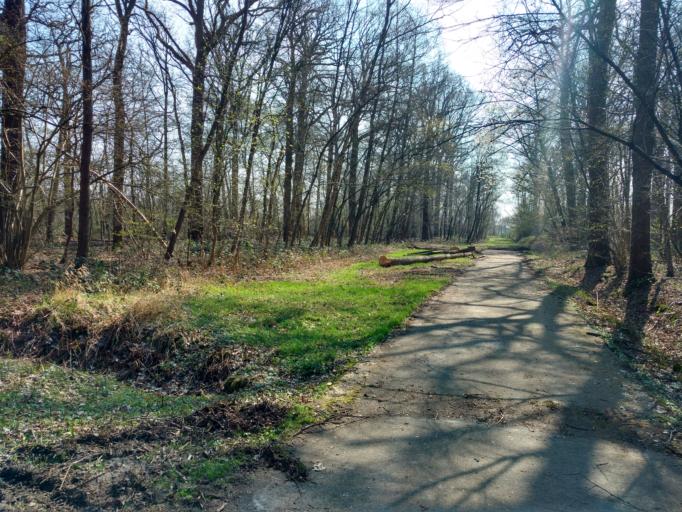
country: BE
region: Flanders
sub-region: Provincie Oost-Vlaanderen
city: Waarschoot
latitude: 51.1594
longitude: 3.5791
